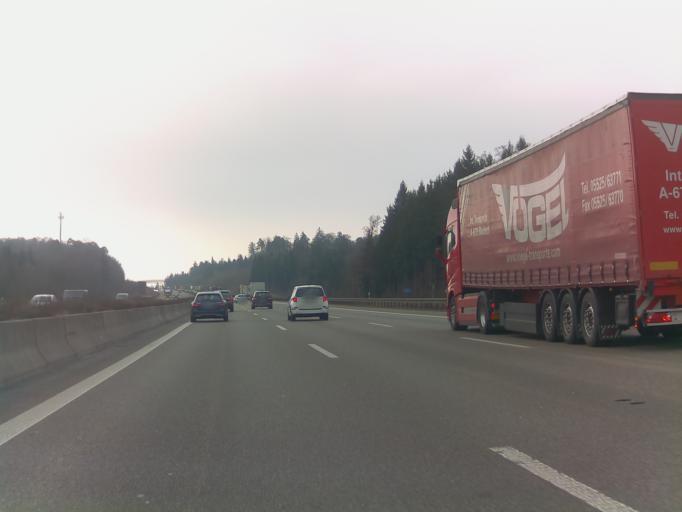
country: DE
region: Baden-Wuerttemberg
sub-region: Karlsruhe Region
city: Wurmberg
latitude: 48.8663
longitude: 8.7919
